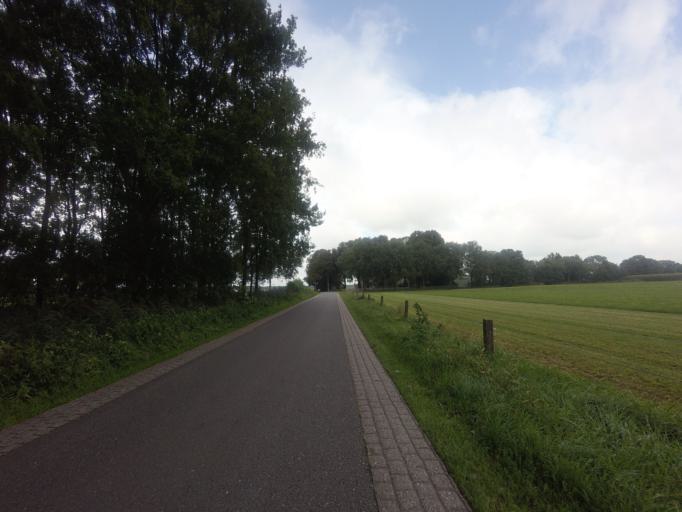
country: NL
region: Friesland
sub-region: Gemeente Skarsterlan
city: Oudehaske
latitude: 52.9371
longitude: 5.8497
